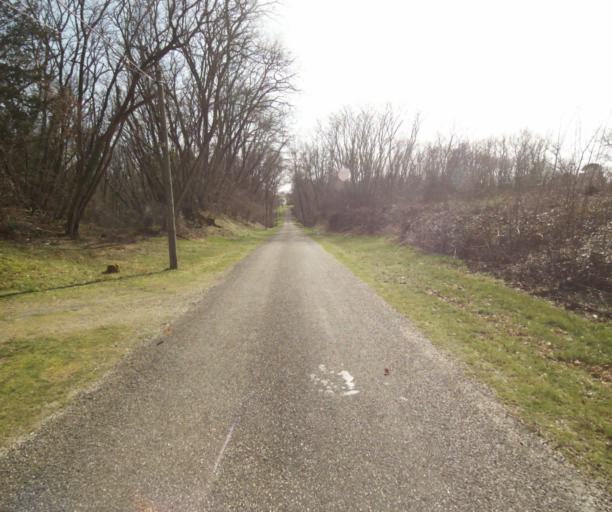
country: FR
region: Aquitaine
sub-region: Departement des Landes
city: Roquefort
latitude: 44.1240
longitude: -0.1917
